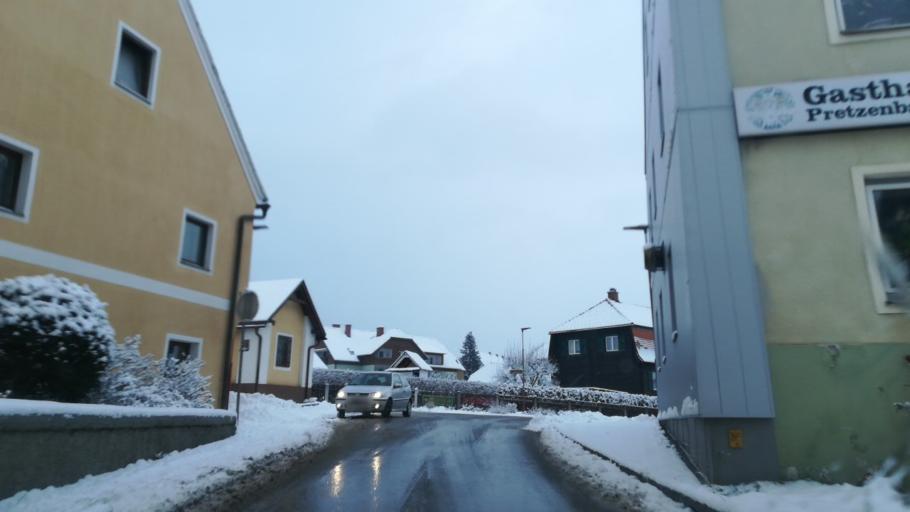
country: AT
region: Styria
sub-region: Politischer Bezirk Murtal
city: Fohnsdorf
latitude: 47.2067
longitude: 14.6605
